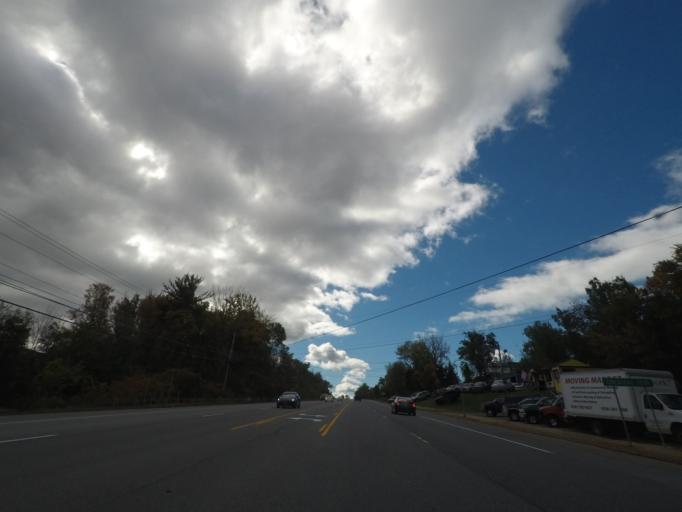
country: US
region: New York
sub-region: Albany County
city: Cohoes
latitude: 42.8117
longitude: -73.7320
